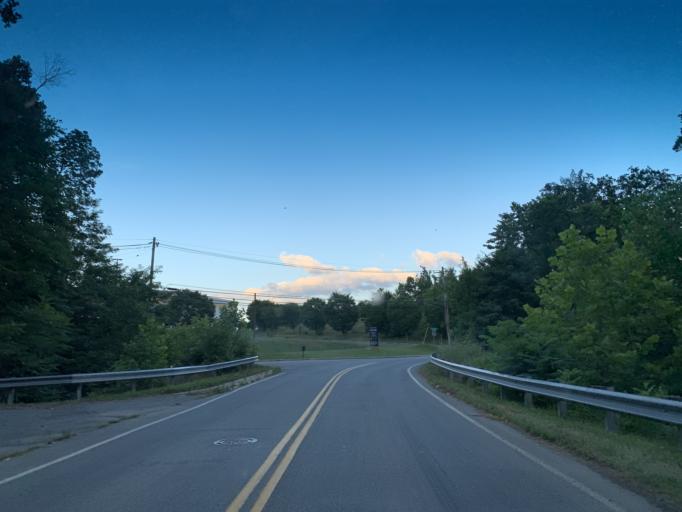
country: US
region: Maryland
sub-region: Harford County
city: Aberdeen
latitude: 39.5282
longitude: -76.1438
